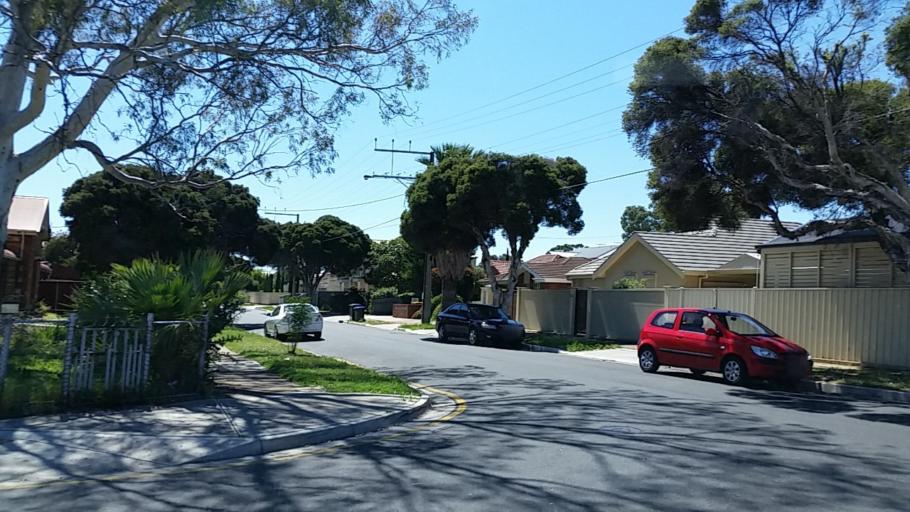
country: AU
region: South Australia
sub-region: Charles Sturt
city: Woodville North
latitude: -34.8714
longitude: 138.5423
